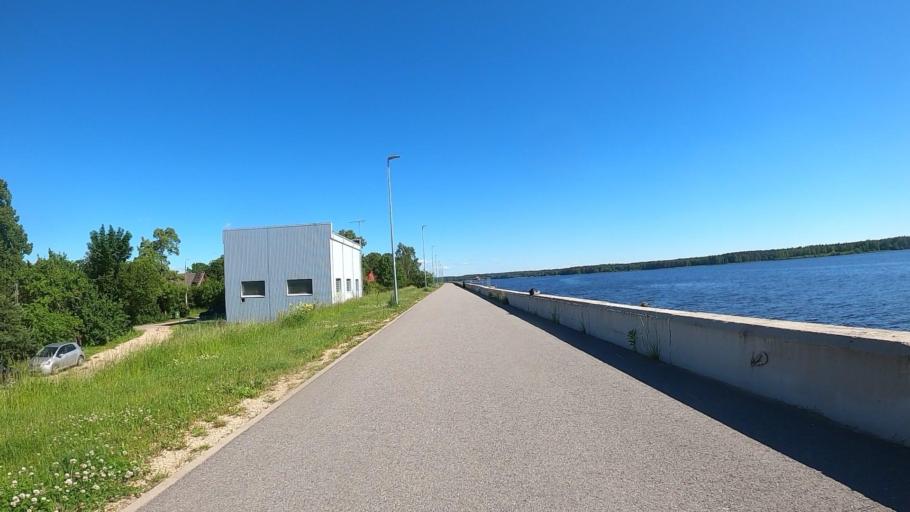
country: LV
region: Ikskile
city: Ikskile
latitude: 56.8270
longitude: 24.4881
